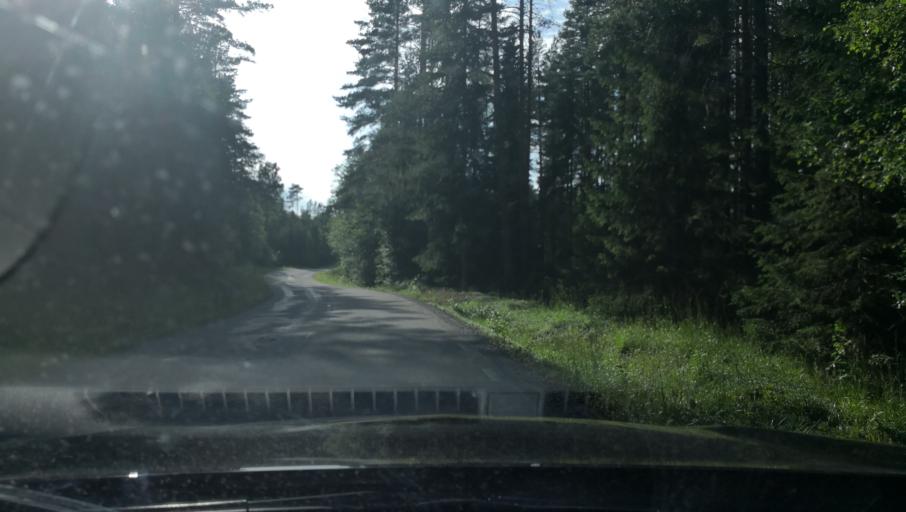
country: SE
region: Dalarna
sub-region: Smedjebackens Kommun
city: Smedjebacken
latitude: 59.9809
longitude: 15.3849
